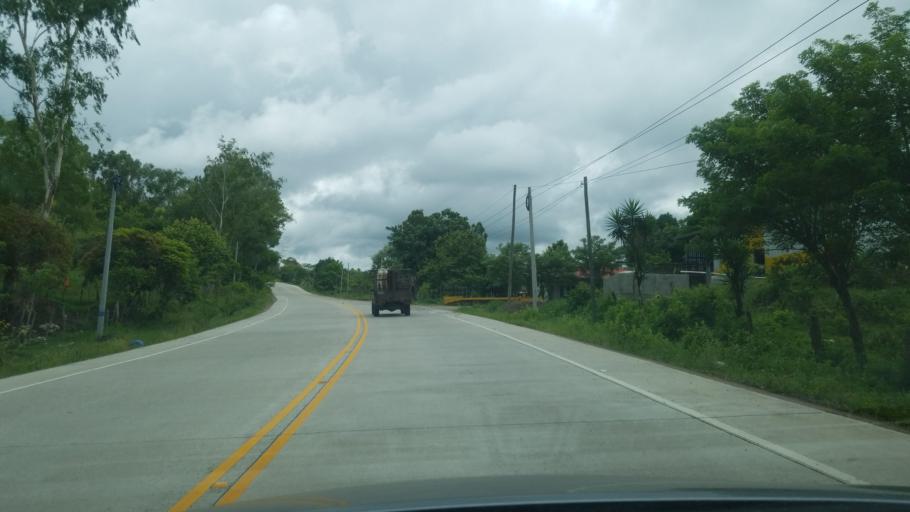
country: HN
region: Copan
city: San Jeronimo
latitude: 14.9810
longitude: -88.8794
